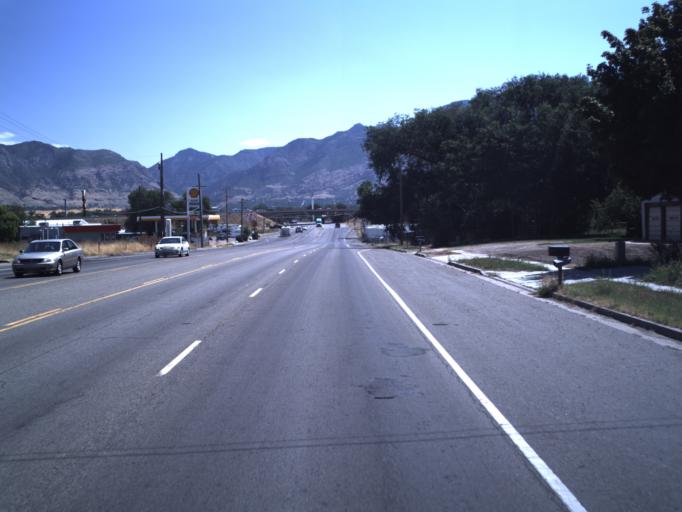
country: US
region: Utah
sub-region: Weber County
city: Marriott-Slaterville
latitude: 41.2287
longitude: -112.0190
